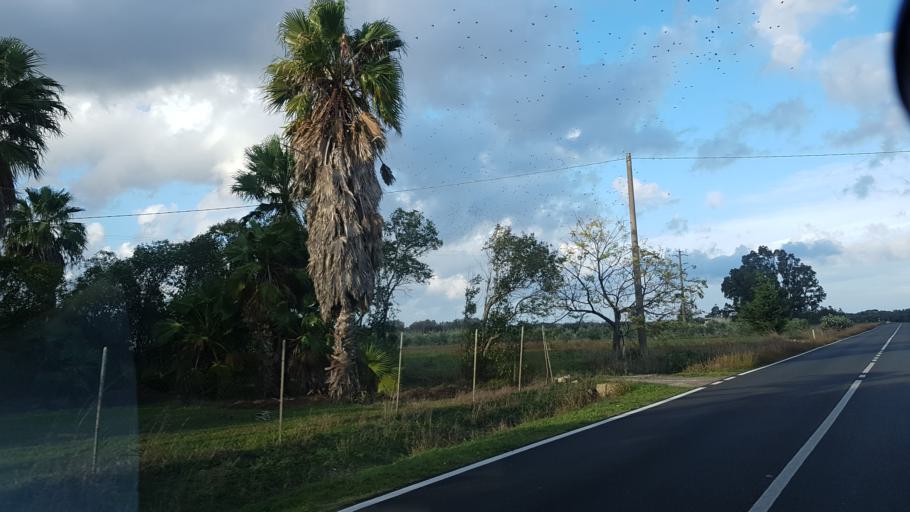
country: IT
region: Apulia
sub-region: Provincia di Brindisi
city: San Pietro Vernotico
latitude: 40.5015
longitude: 18.0054
